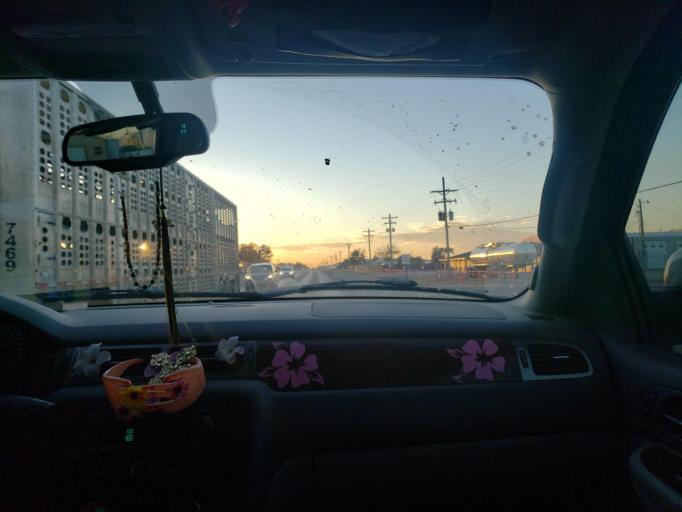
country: US
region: Kansas
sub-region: Finney County
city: Garden City
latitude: 37.9895
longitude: -100.9202
